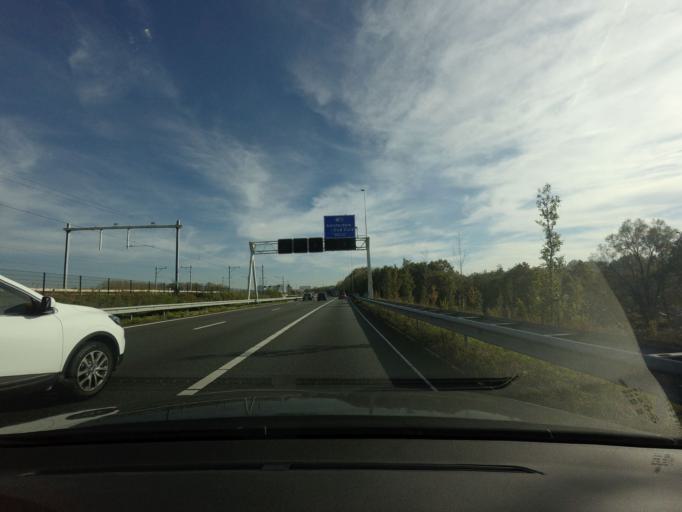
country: NL
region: North Holland
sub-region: Gemeente Amstelveen
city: Amstelveen
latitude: 52.3377
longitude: 4.8388
